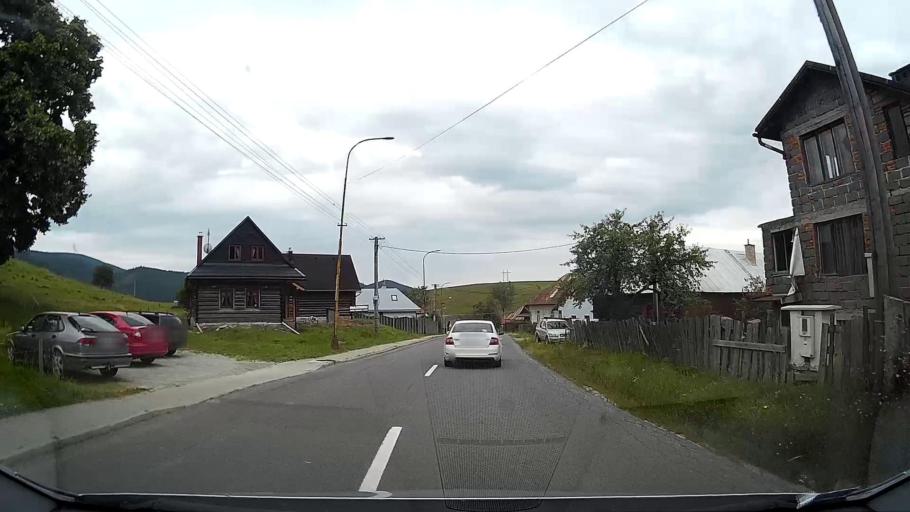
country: SK
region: Banskobystricky
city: Revuca
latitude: 48.8477
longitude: 20.1845
